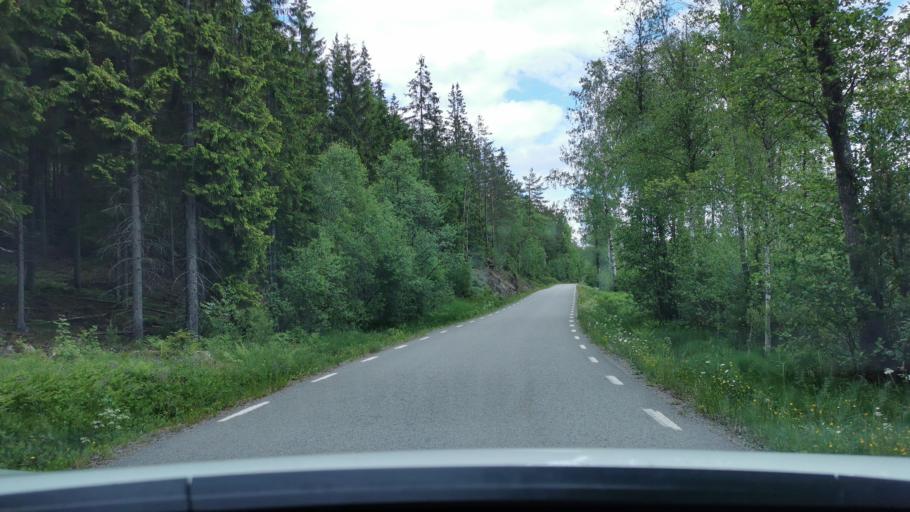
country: SE
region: Vaestra Goetaland
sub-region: Bengtsfors Kommun
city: Dals Langed
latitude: 58.8585
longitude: 12.3270
